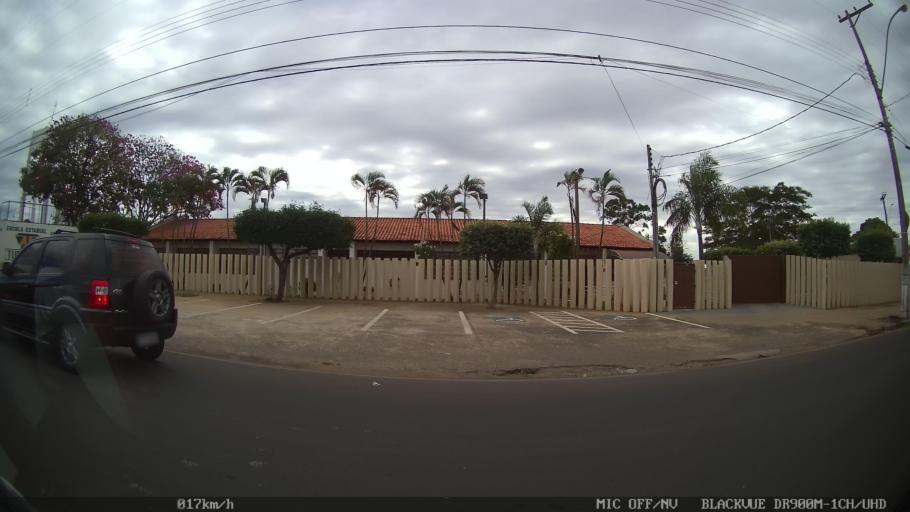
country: BR
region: Sao Paulo
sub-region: Bady Bassitt
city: Bady Bassitt
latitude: -20.8140
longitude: -49.4976
